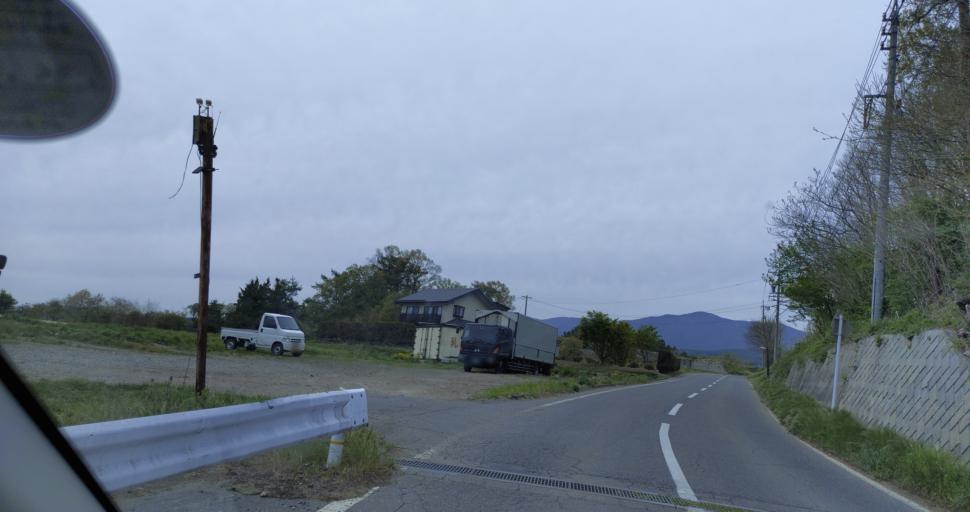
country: JP
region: Nagano
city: Komoro
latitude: 36.3246
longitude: 138.4886
